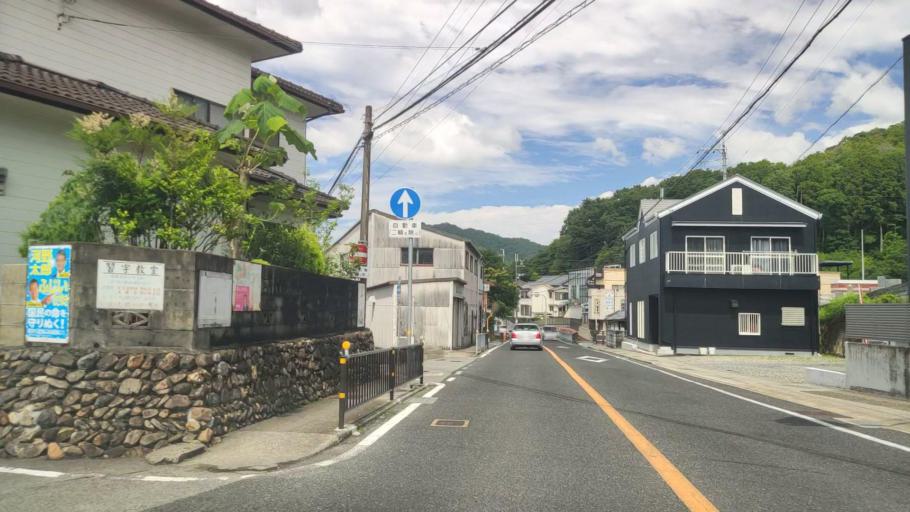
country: JP
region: Hyogo
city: Nishiwaki
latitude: 34.9911
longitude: 134.9759
